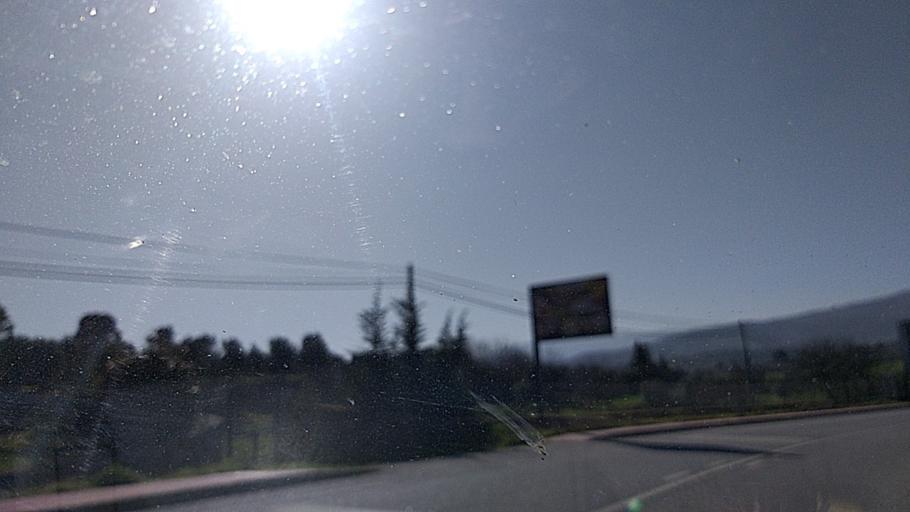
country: PT
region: Guarda
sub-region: Celorico da Beira
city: Celorico da Beira
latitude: 40.6567
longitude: -7.3809
